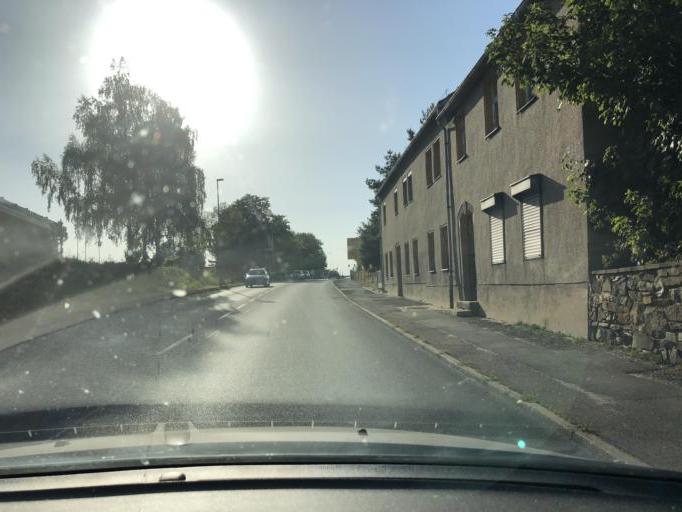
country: DE
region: Saxony
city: Oschatz
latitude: 51.3020
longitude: 13.1000
